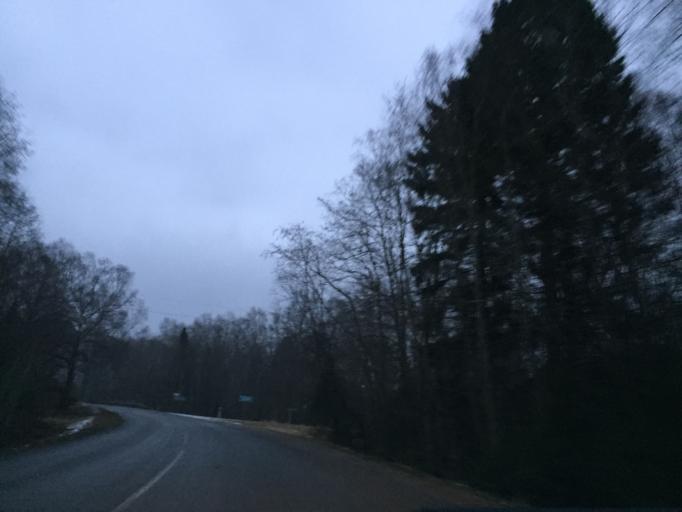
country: EE
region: Saare
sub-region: Kuressaare linn
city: Kuressaare
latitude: 58.5713
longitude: 22.6705
